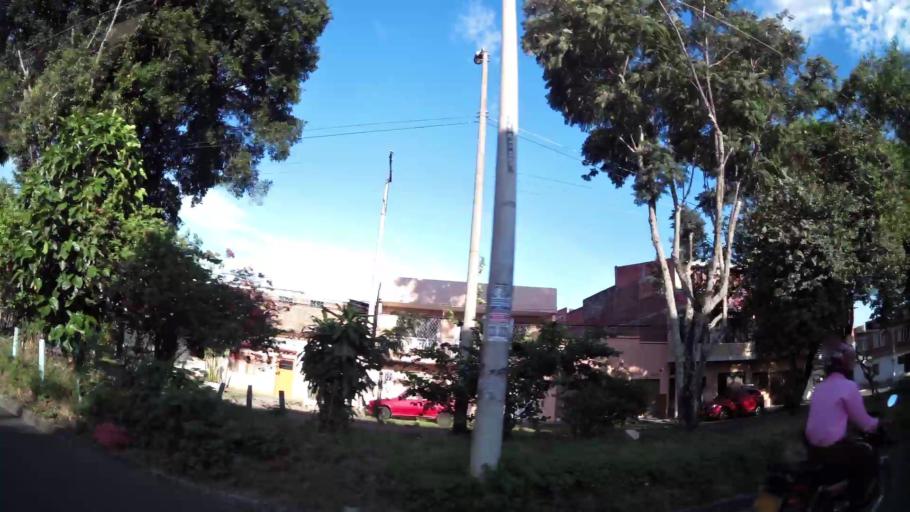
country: CO
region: Valle del Cauca
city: Cali
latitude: 3.4304
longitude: -76.5166
